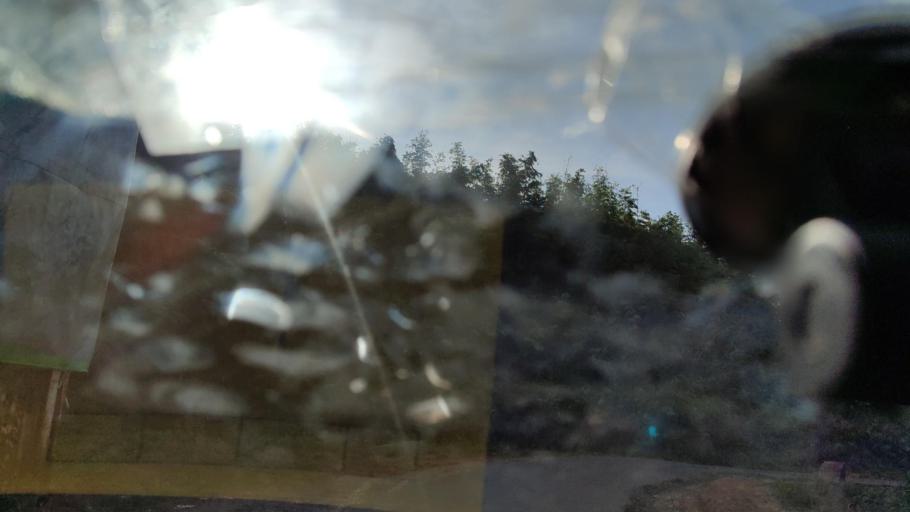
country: MM
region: Magway
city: Minbu
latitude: 19.8706
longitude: 94.2006
